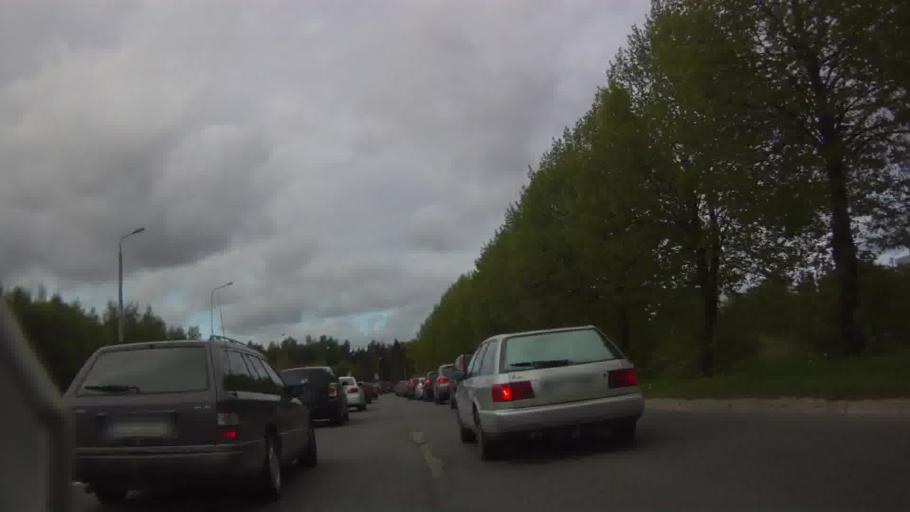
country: LV
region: Stopini
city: Ulbroka
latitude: 56.9572
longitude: 24.2279
